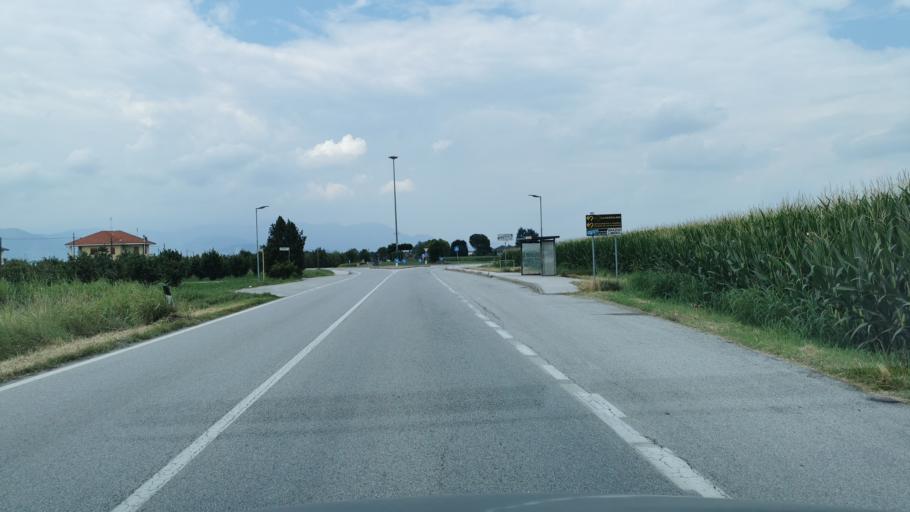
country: IT
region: Piedmont
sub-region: Provincia di Torino
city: Garzigliana
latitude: 44.8154
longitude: 7.3714
